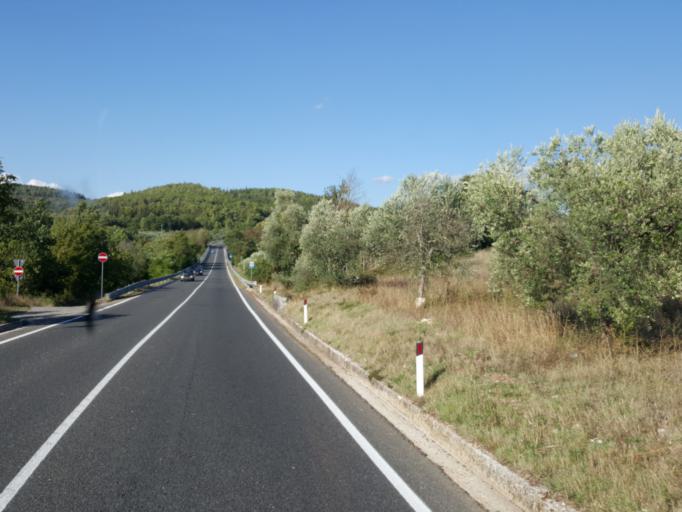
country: IT
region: Molise
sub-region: Provincia di Isernia
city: Macchia d'Isernia
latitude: 41.5460
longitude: 14.1597
